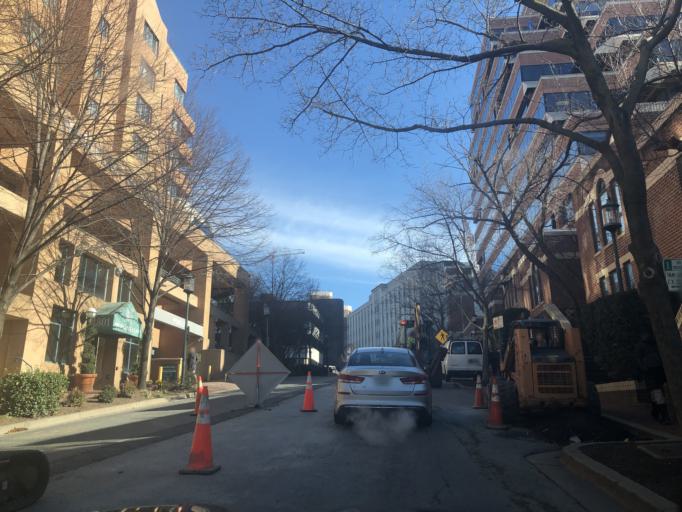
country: US
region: Maryland
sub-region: Montgomery County
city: Bethesda
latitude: 38.9827
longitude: -77.0958
